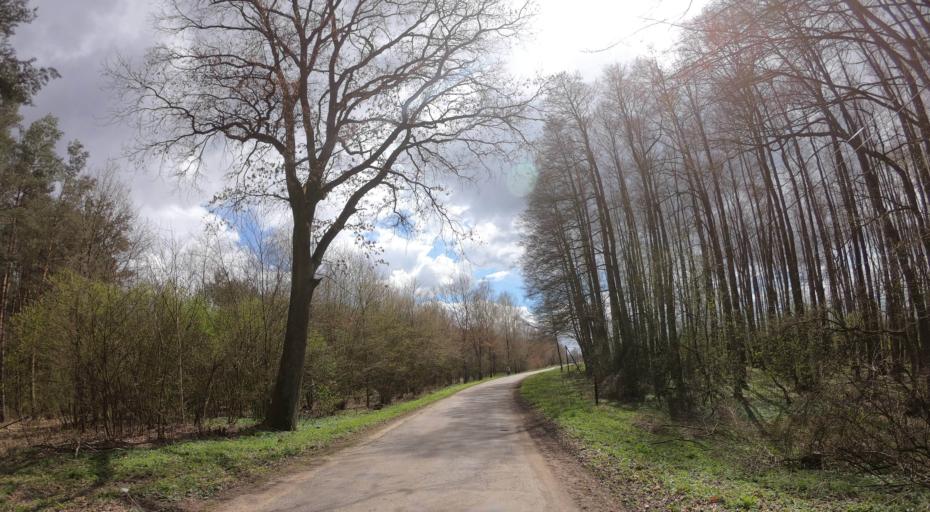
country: PL
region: West Pomeranian Voivodeship
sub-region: Powiat drawski
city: Drawsko Pomorskie
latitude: 53.5346
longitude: 15.8864
